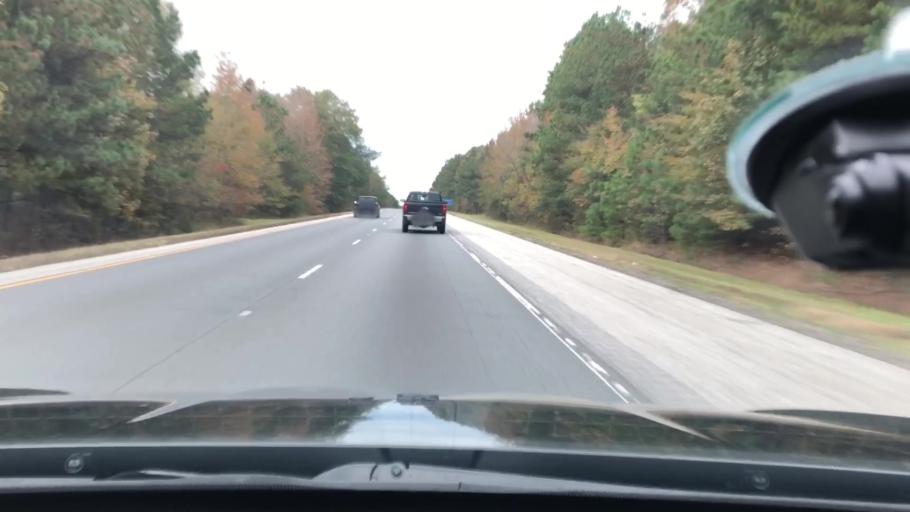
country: US
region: Arkansas
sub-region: Clark County
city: Arkadelphia
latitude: 34.1022
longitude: -93.1016
